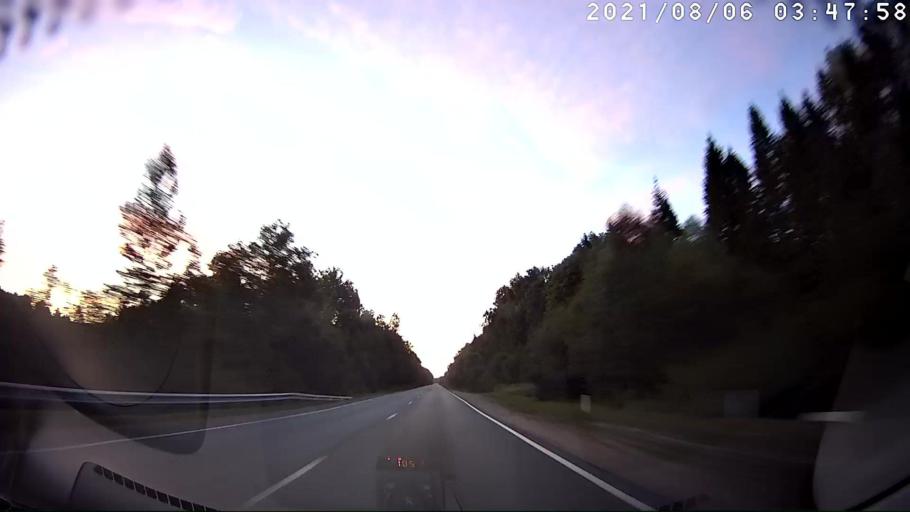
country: RU
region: Tatarstan
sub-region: Zelenodol'skiy Rayon
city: Zelenodolsk
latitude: 55.8846
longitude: 48.4743
